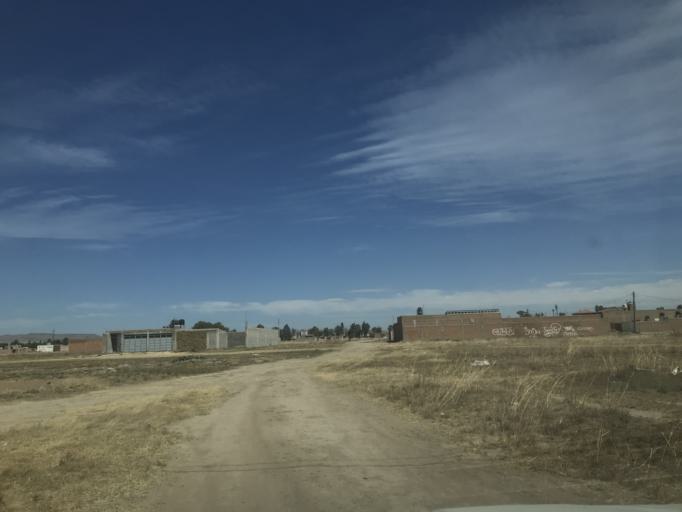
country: MX
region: Durango
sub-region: Durango
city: Sebastian Lerdo de Tejada
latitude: 23.9767
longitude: -104.6532
